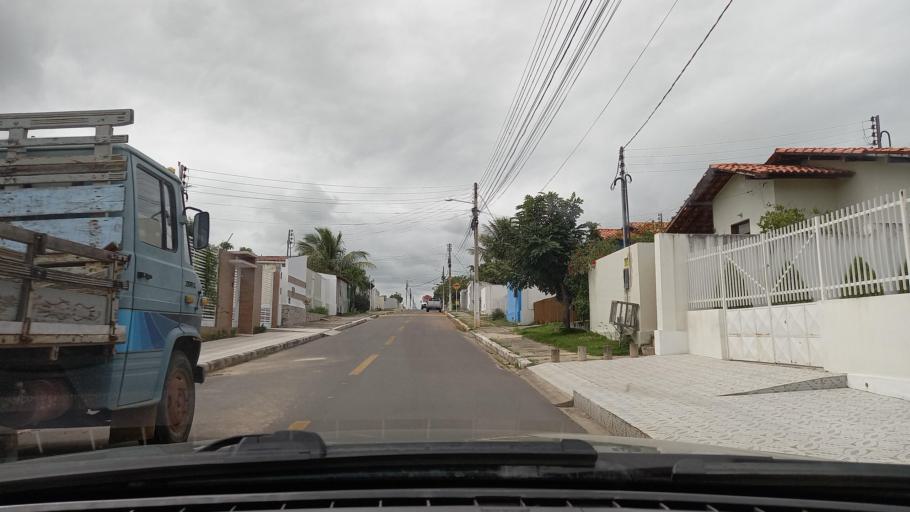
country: BR
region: Sergipe
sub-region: Caninde De Sao Francisco
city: Caninde de Sao Francisco
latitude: -9.6146
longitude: -37.7664
